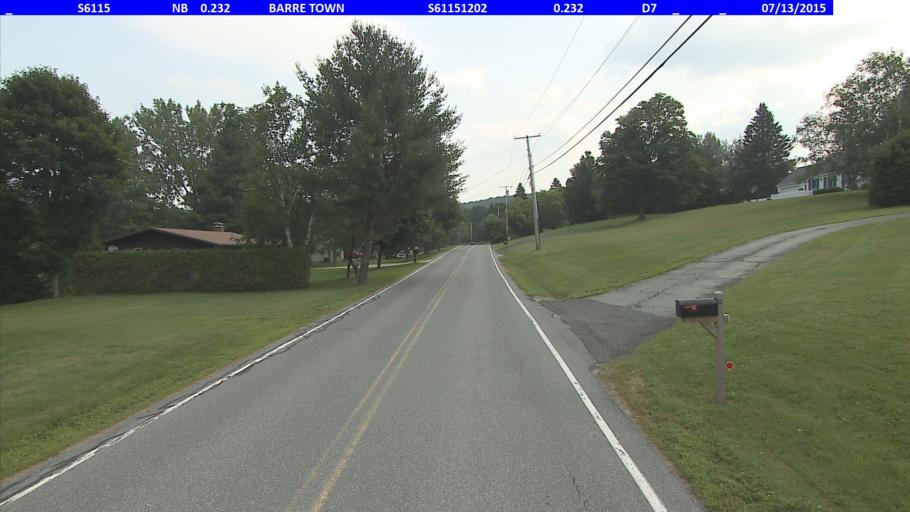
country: US
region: Vermont
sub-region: Washington County
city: Barre
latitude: 44.2034
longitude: -72.4850
